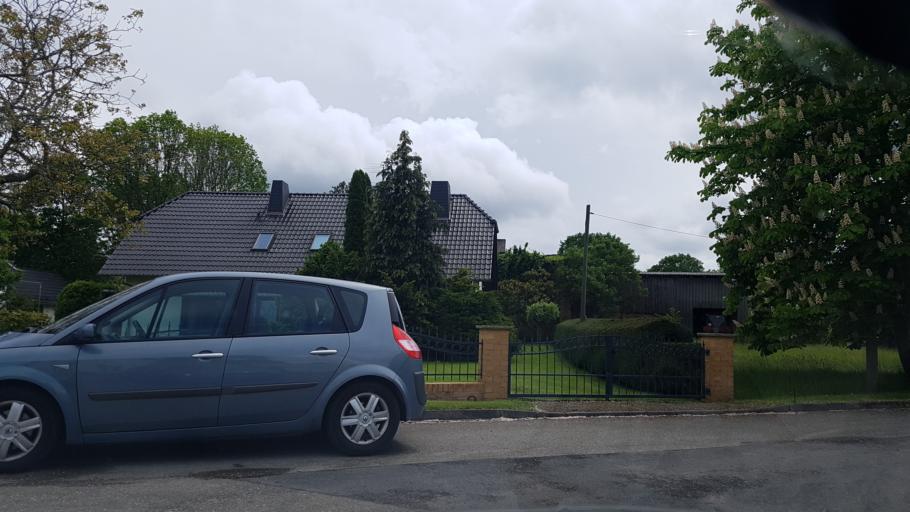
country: DE
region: Brandenburg
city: Drahnsdorf
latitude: 51.8176
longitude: 13.6046
